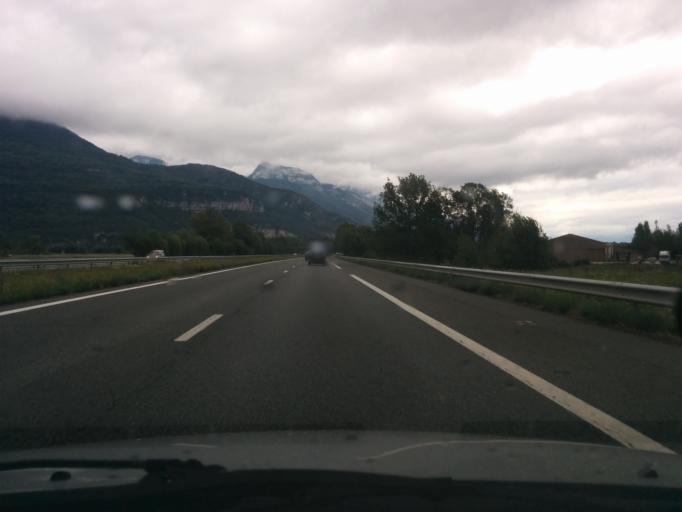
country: FR
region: Rhone-Alpes
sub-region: Departement de l'Isere
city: Saint-Jean-de-Moirans
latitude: 45.3244
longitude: 5.6010
